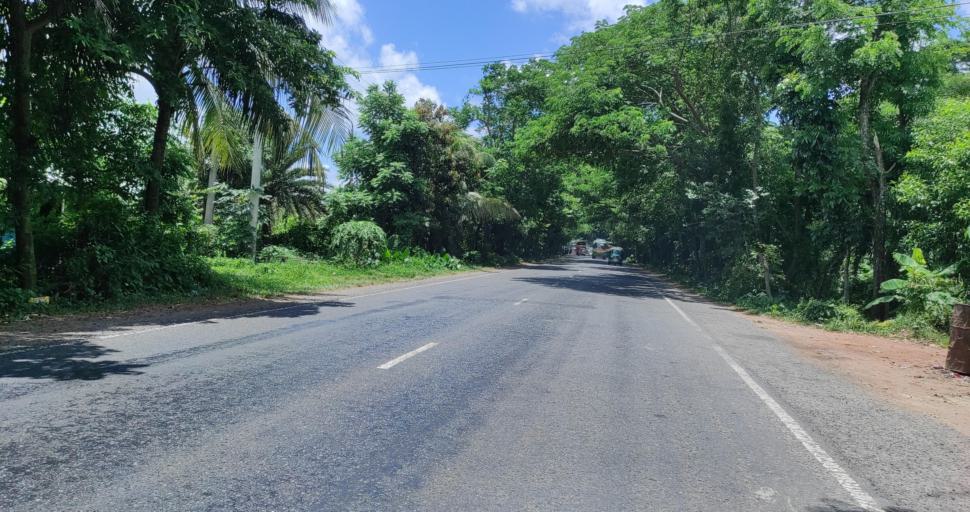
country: BD
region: Barisal
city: Gaurnadi
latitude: 22.8335
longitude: 90.2548
